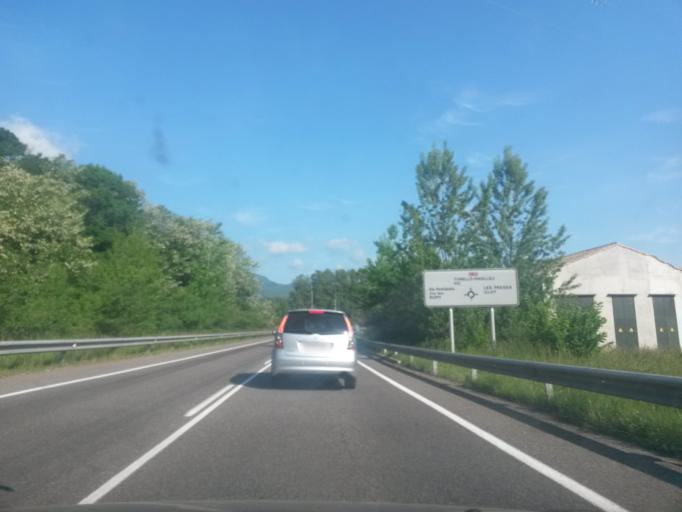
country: ES
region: Catalonia
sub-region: Provincia de Girona
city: Bas
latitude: 42.1274
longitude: 2.4505
